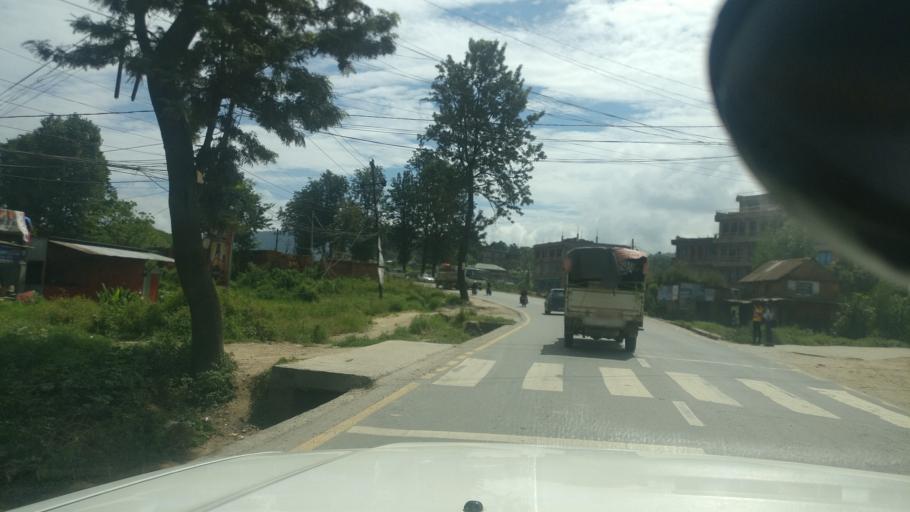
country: NP
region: Central Region
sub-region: Bagmati Zone
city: Bhaktapur
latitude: 27.6612
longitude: 85.4463
